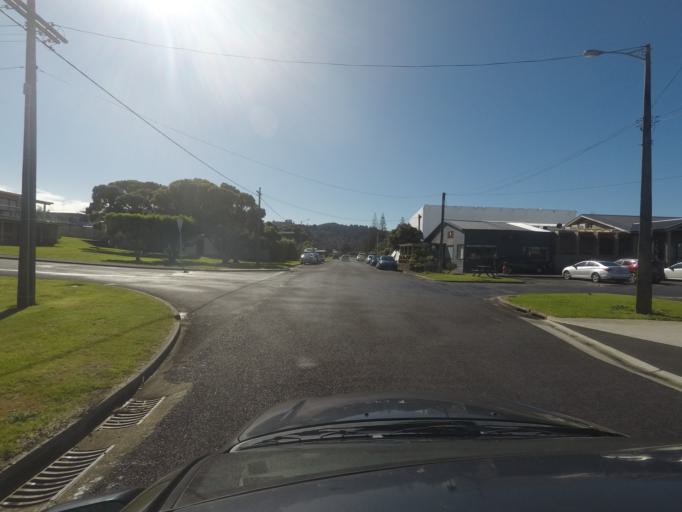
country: NZ
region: Bay of Plenty
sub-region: Western Bay of Plenty District
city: Waihi Beach
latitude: -37.4060
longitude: 175.9431
